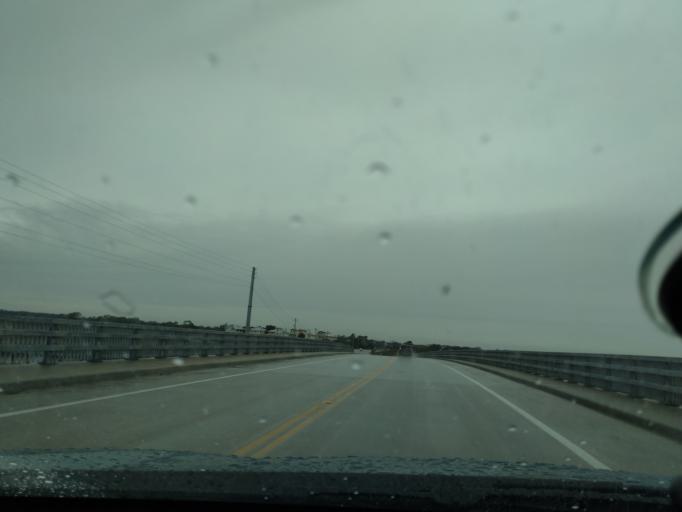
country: US
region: South Carolina
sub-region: Charleston County
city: Folly Beach
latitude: 32.6755
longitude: -79.9506
